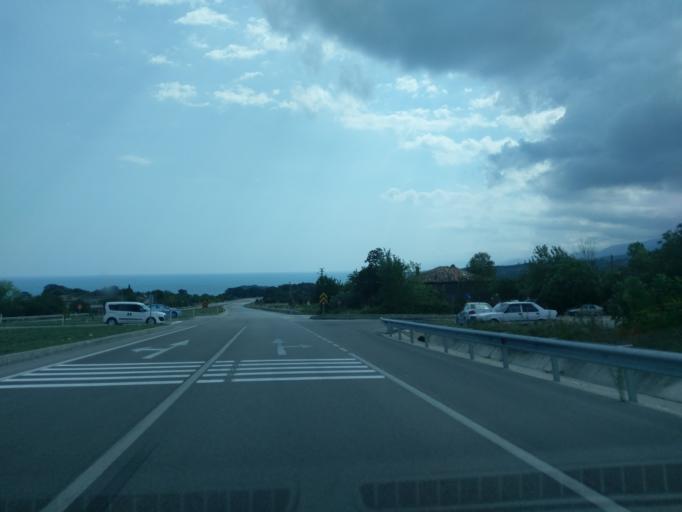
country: TR
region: Sinop
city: Kabali
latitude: 41.8474
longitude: 35.1309
